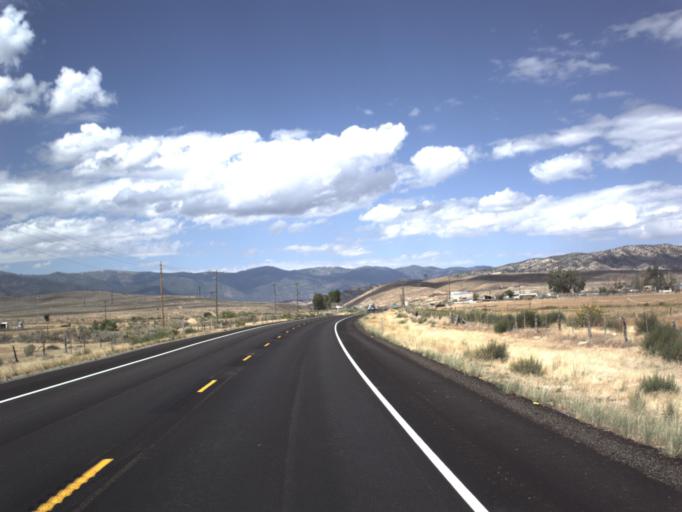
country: US
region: Utah
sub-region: Sevier County
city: Aurora
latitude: 38.9558
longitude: -111.9169
